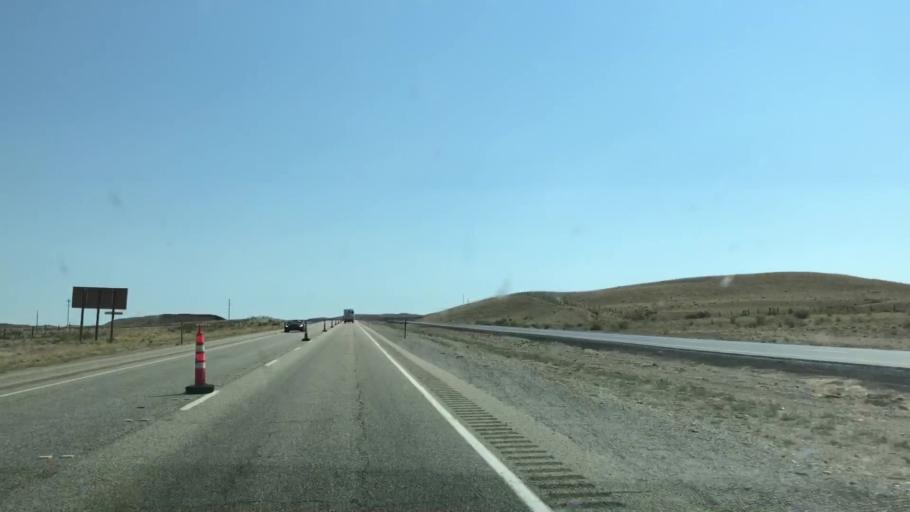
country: US
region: Wyoming
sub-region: Carbon County
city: Rawlins
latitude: 41.7492
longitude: -106.9413
